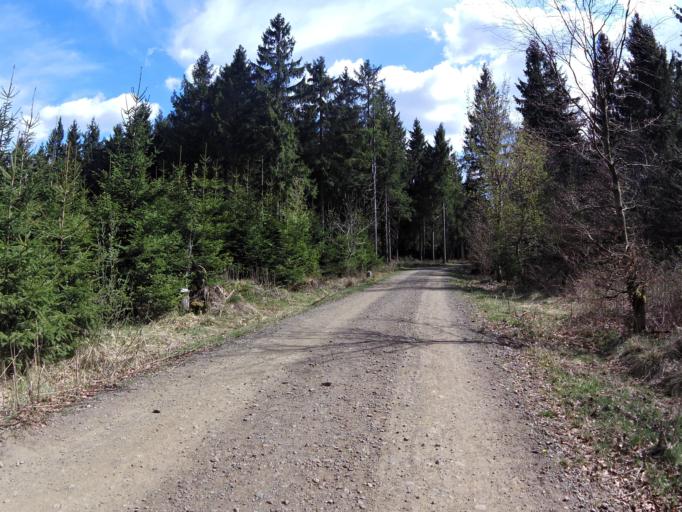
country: DE
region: Thuringia
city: Tambach-Dietharz
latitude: 50.7818
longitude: 10.5621
